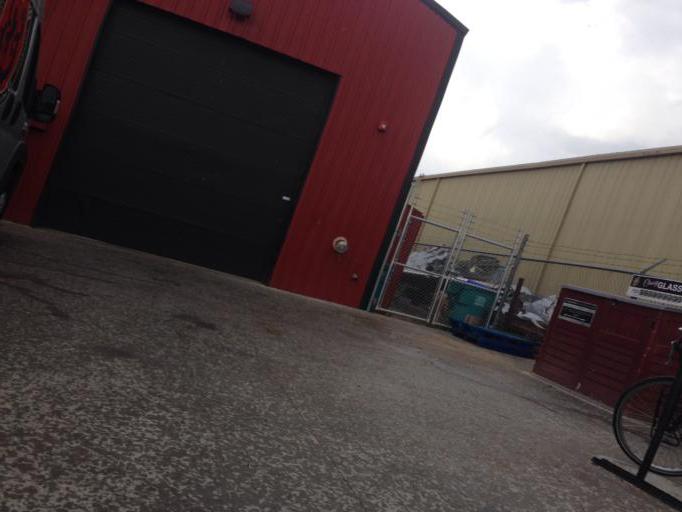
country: US
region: Colorado
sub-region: Larimer County
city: Fort Collins
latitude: 40.5893
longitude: -105.0458
